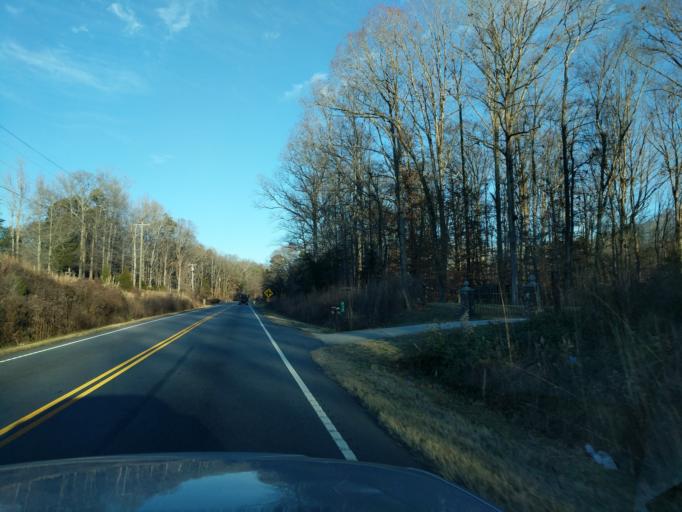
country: US
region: South Carolina
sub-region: Greenville County
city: Simpsonville
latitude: 34.6539
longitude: -82.2947
